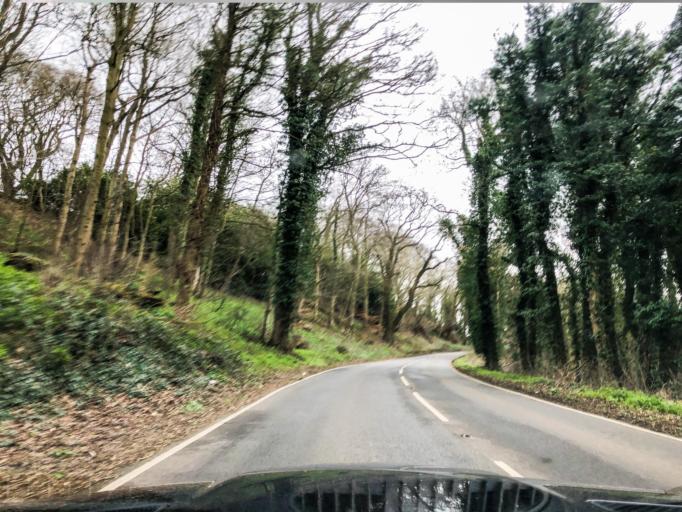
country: GB
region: England
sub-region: Oxfordshire
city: Hanwell
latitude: 52.1335
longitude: -1.4452
